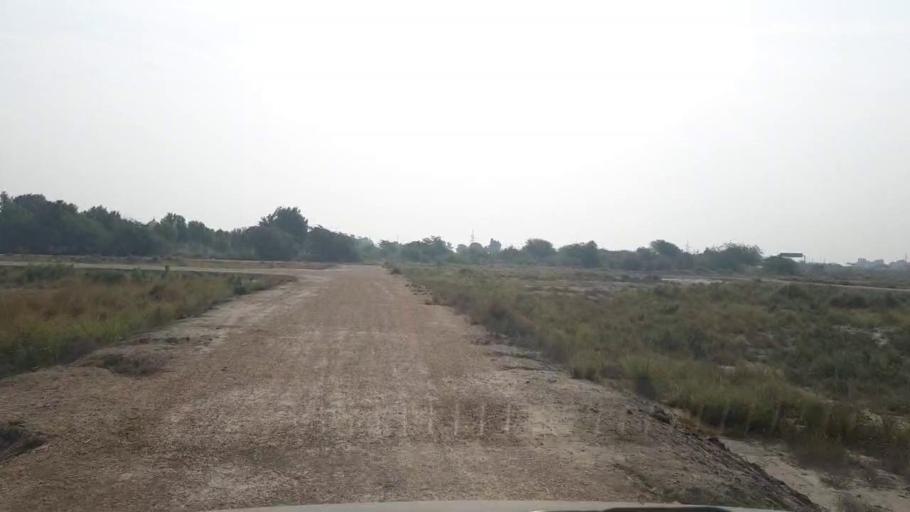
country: PK
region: Sindh
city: Tando Muhammad Khan
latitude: 25.1345
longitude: 68.5194
